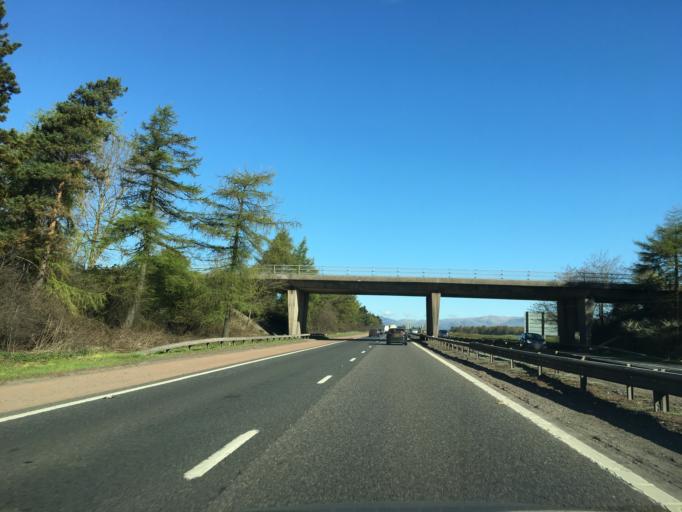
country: GB
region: Scotland
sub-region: Falkirk
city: Falkirk
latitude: 56.0286
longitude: -3.7626
